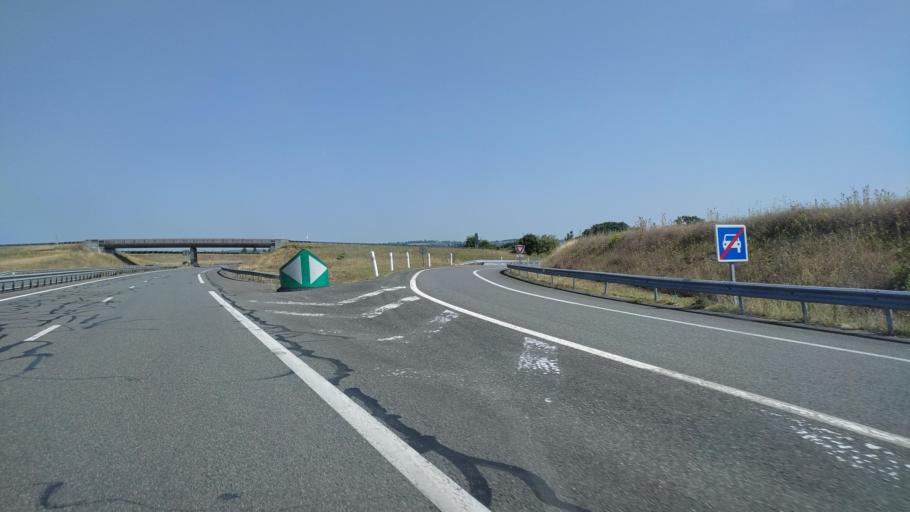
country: FR
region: Poitou-Charentes
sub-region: Departement de la Charente
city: Saint-Meme-les-Carrieres
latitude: 45.6919
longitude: -0.0892
